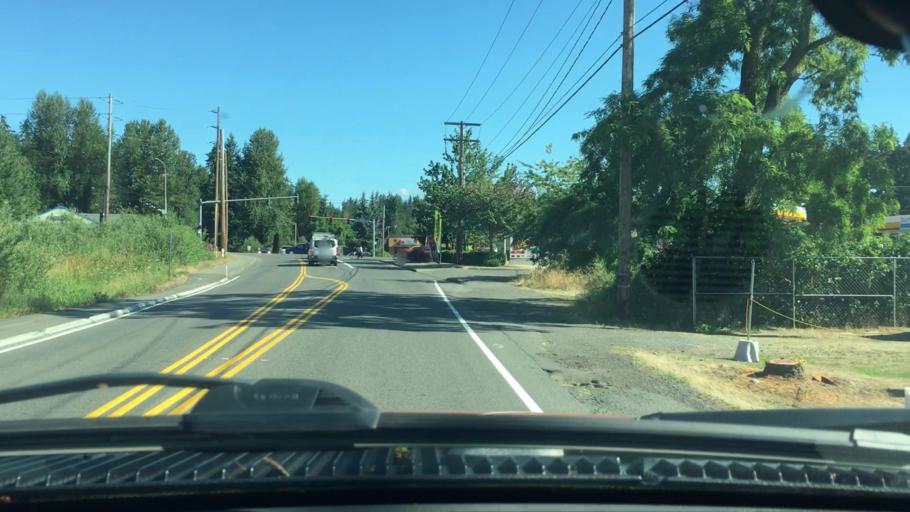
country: US
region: Washington
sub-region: King County
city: Covington
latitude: 47.3571
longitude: -122.1389
